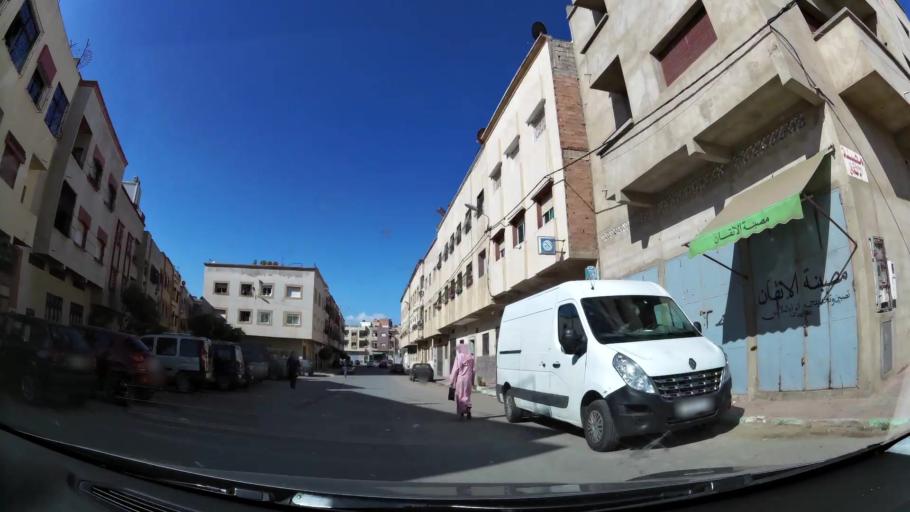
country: MA
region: Rabat-Sale-Zemmour-Zaer
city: Sale
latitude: 34.0565
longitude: -6.8125
